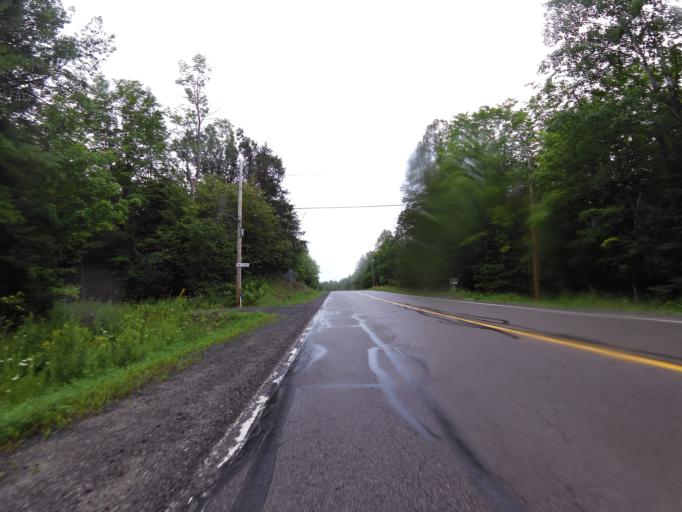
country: CA
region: Ontario
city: Perth
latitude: 44.9990
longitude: -76.3791
